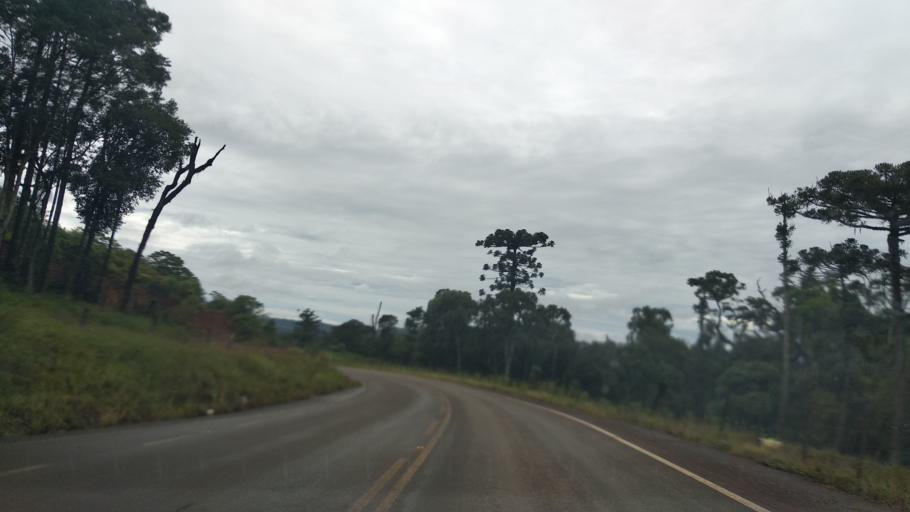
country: BR
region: Santa Catarina
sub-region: Videira
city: Videira
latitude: -27.0285
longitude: -51.1592
